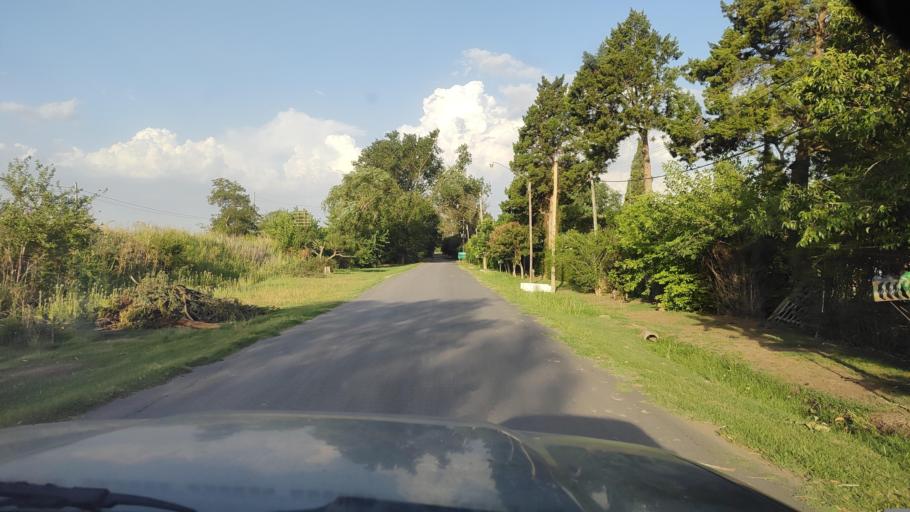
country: AR
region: Buenos Aires
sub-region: Partido de Lujan
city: Lujan
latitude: -34.5484
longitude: -59.1922
